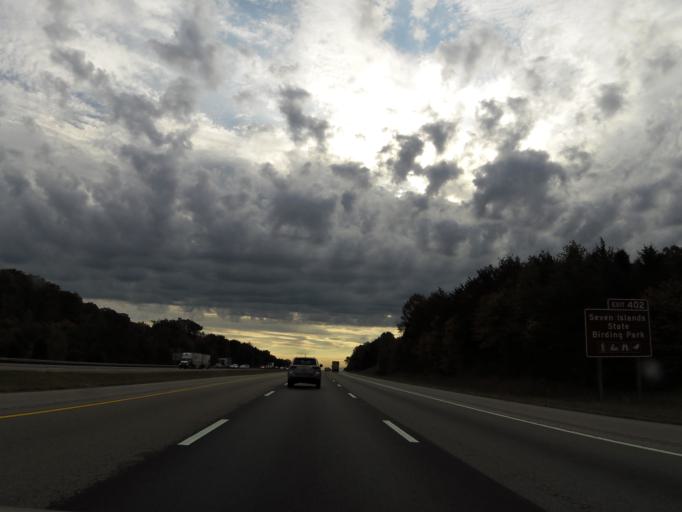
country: US
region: Tennessee
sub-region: Knox County
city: Mascot
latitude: 36.0025
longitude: -83.7370
